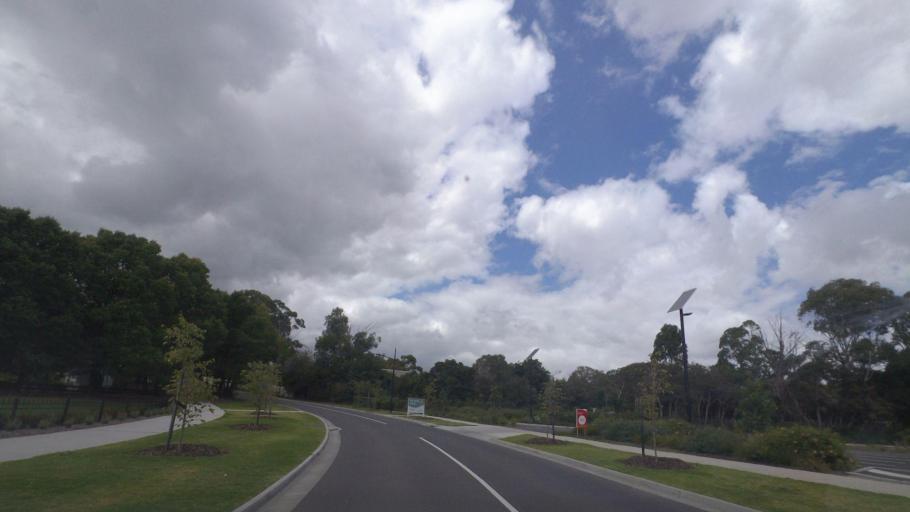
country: AU
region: Victoria
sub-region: Knox
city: Scoresby
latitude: -37.9148
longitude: 145.2328
